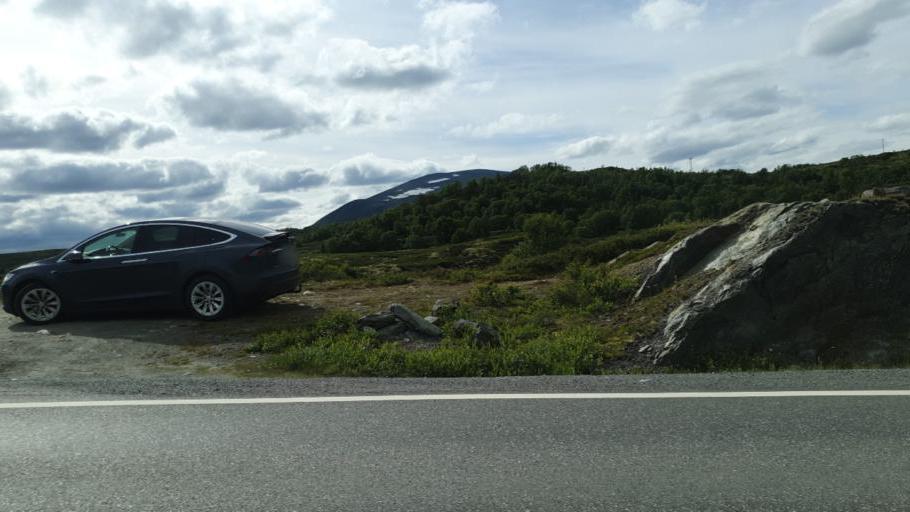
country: NO
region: Sor-Trondelag
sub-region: Oppdal
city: Oppdal
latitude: 62.2839
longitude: 9.5997
